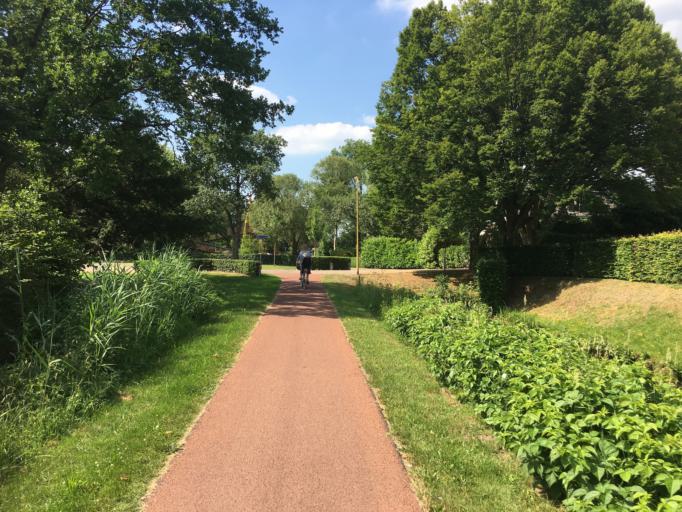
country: NL
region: Friesland
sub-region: Gemeente Heerenveen
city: Oranjewoud
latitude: 52.9506
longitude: 5.9389
